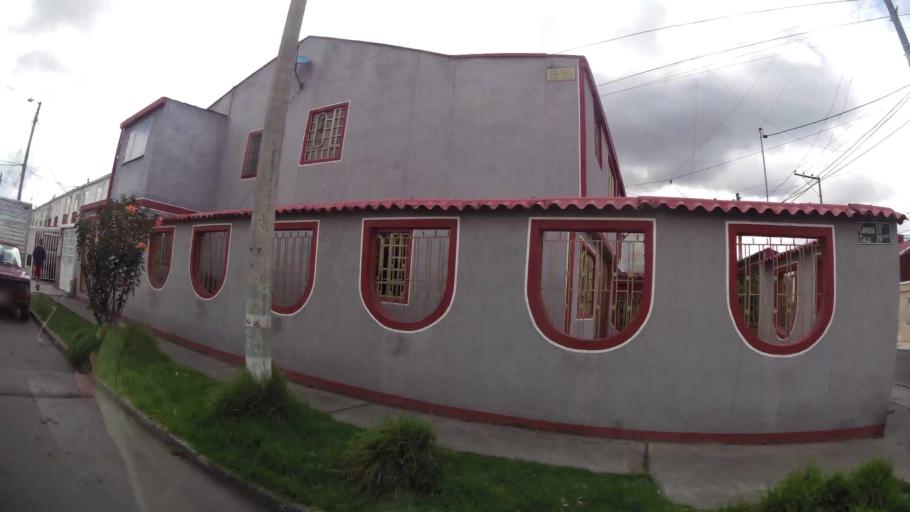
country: CO
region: Bogota D.C.
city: Bogota
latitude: 4.5984
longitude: -74.1193
